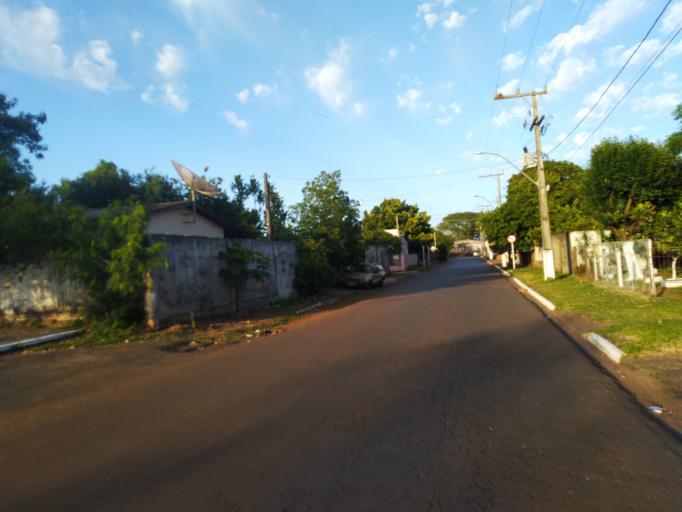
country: BR
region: Rio Grande do Sul
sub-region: Sao Borja
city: Sao Borja
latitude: -28.6501
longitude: -56.0095
